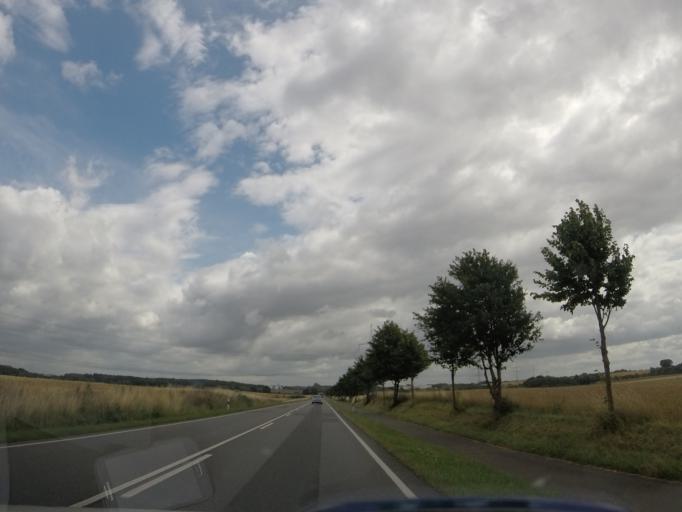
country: DE
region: Mecklenburg-Vorpommern
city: Lalendorf
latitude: 53.7628
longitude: 12.3596
